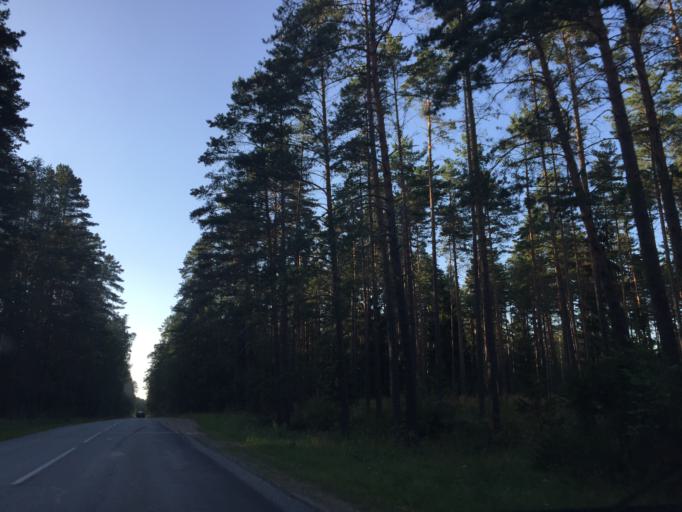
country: LV
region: Garkalne
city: Garkalne
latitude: 57.0168
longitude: 24.4424
